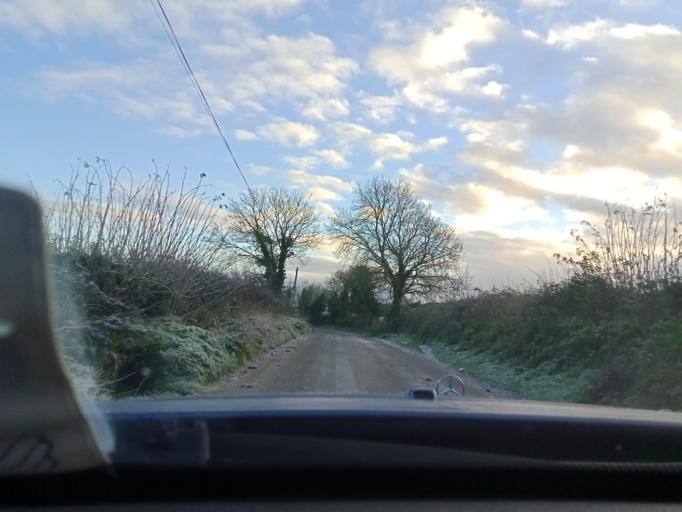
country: IE
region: Leinster
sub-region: County Carlow
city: Bagenalstown
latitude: 52.6383
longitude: -7.0298
